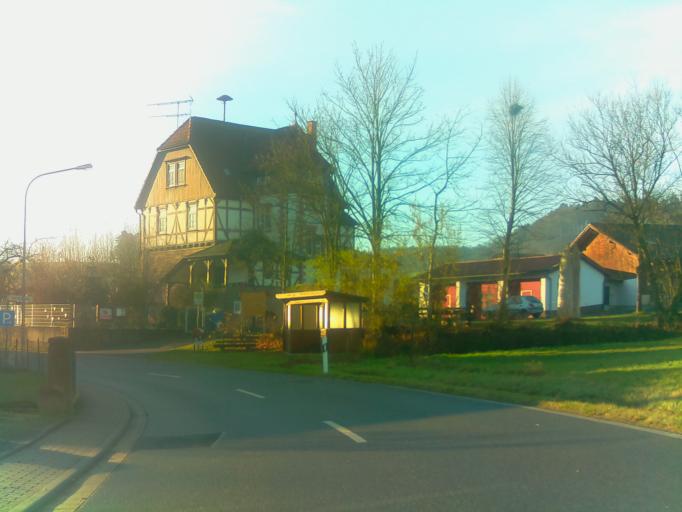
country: DE
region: Hesse
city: Reichelsheim
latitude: 49.6726
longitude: 8.8478
